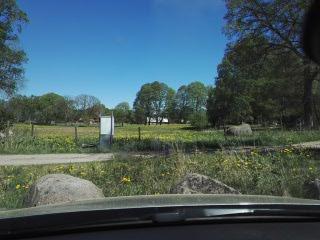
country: SE
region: Kronoberg
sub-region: Vaxjo Kommun
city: Rottne
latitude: 57.0912
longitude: 14.7927
